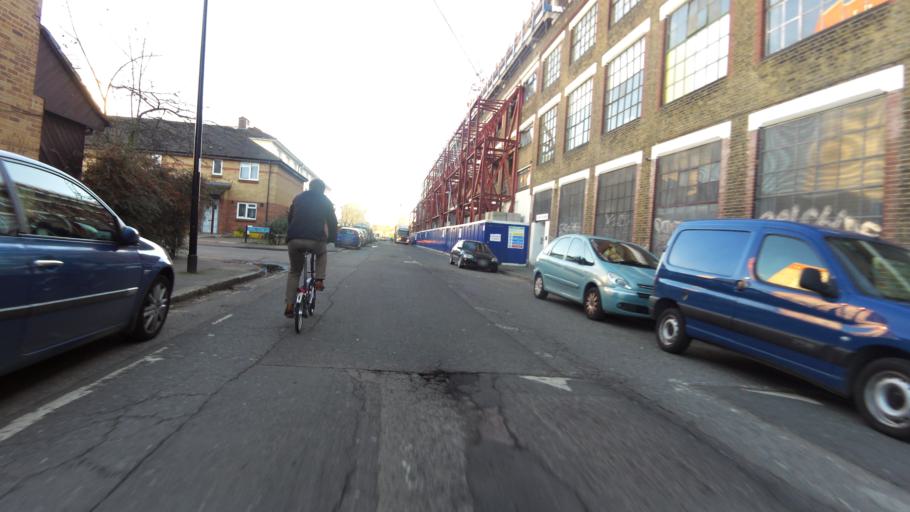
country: GB
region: England
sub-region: Greater London
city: Poplar
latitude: 51.4827
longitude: -0.0354
